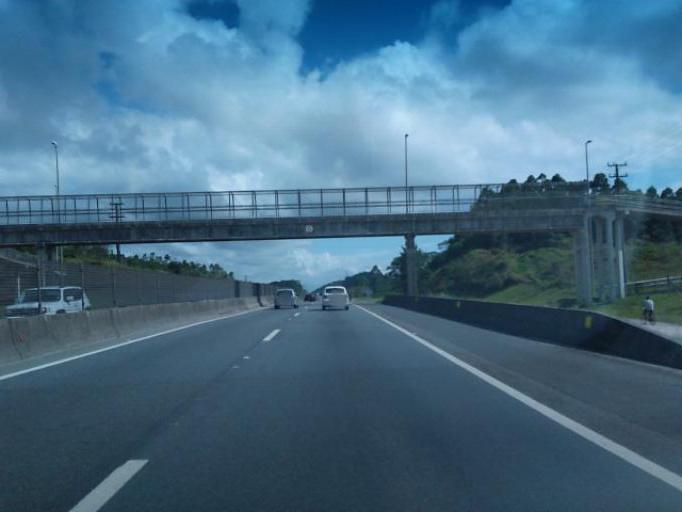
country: BR
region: Santa Catarina
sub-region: Penha
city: Penha
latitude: -26.7276
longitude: -48.7021
